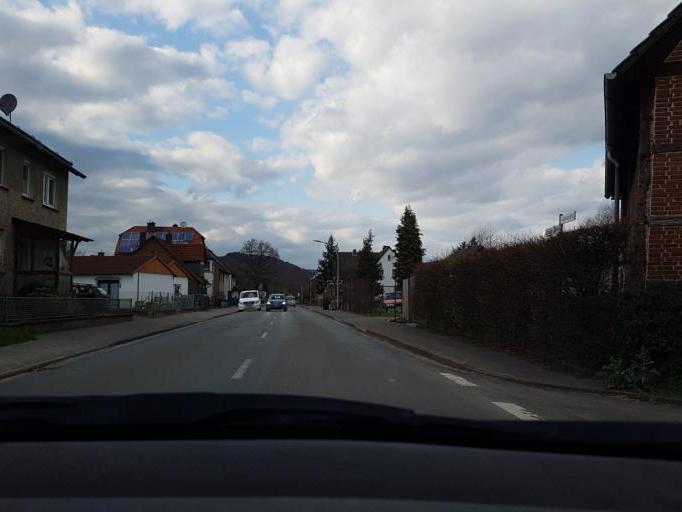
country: DE
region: Lower Saxony
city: Bodenfelde
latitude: 51.6416
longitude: 9.5528
